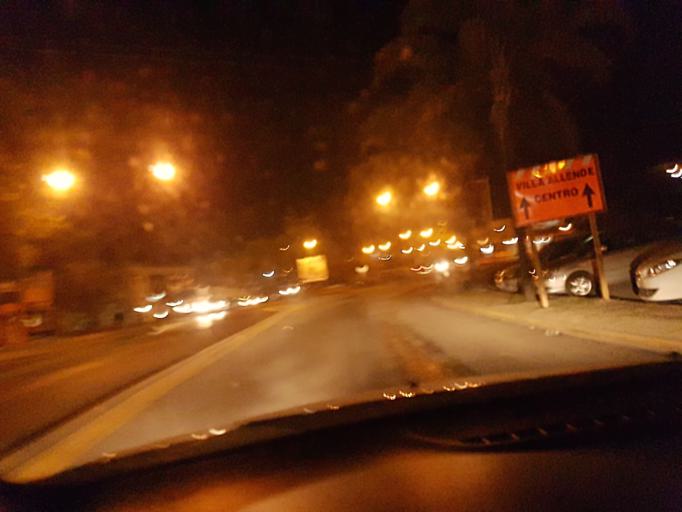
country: AR
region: Cordoba
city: Villa Allende
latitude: -31.2989
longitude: -64.2877
